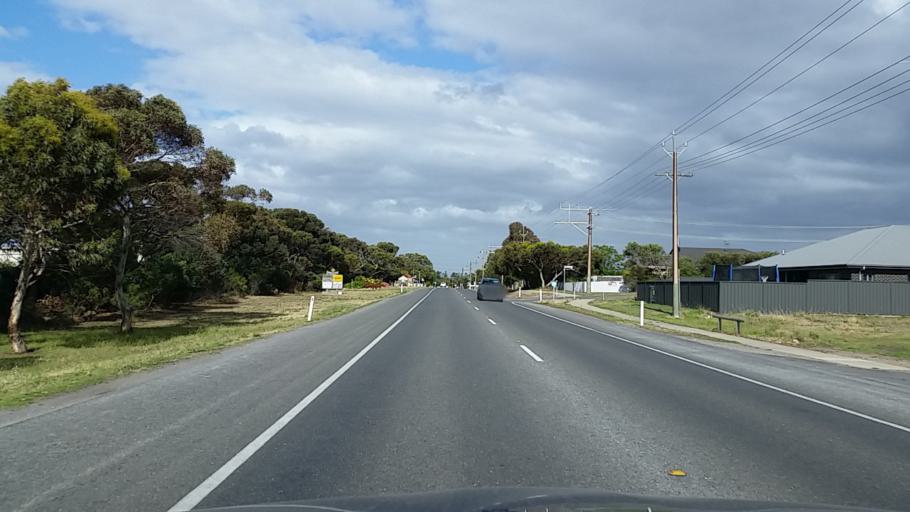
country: AU
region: South Australia
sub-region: Alexandrina
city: Goolwa
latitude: -35.5050
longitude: 138.7720
